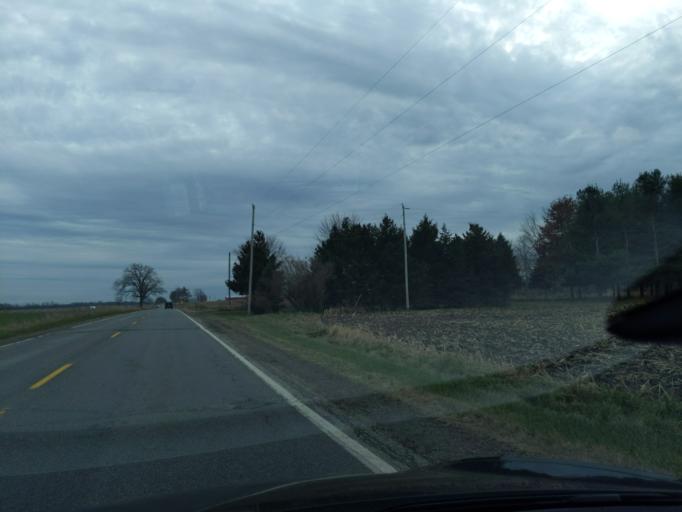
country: US
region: Michigan
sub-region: Ingham County
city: Williamston
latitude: 42.6620
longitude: -84.3637
